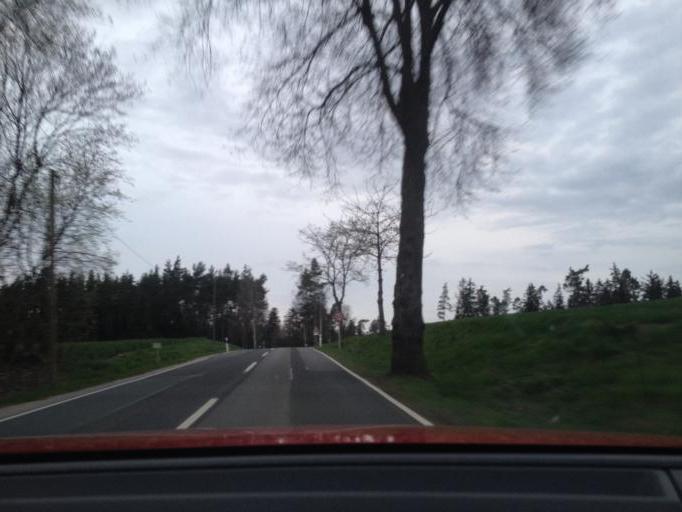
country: DE
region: Bavaria
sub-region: Upper Palatinate
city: Speinshart
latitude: 49.7922
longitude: 11.8210
